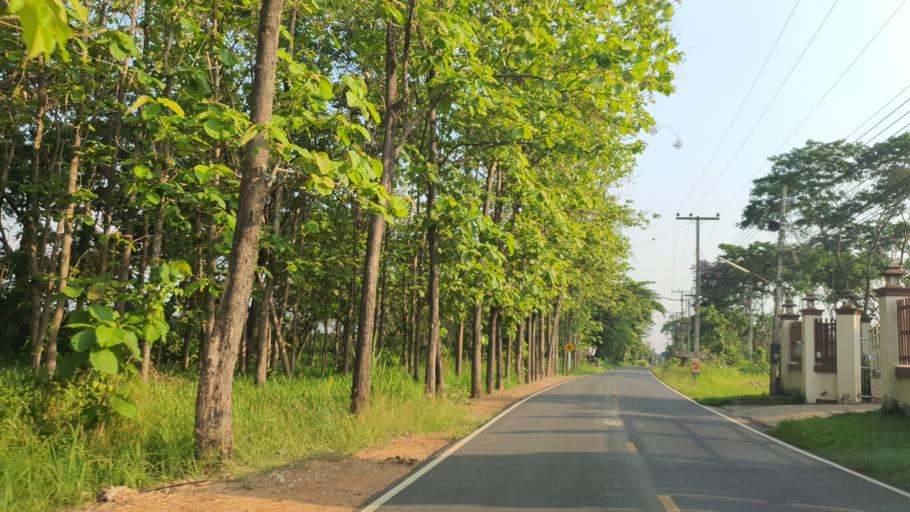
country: TH
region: Chiang Mai
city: Mae Wang
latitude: 18.6096
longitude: 98.8217
